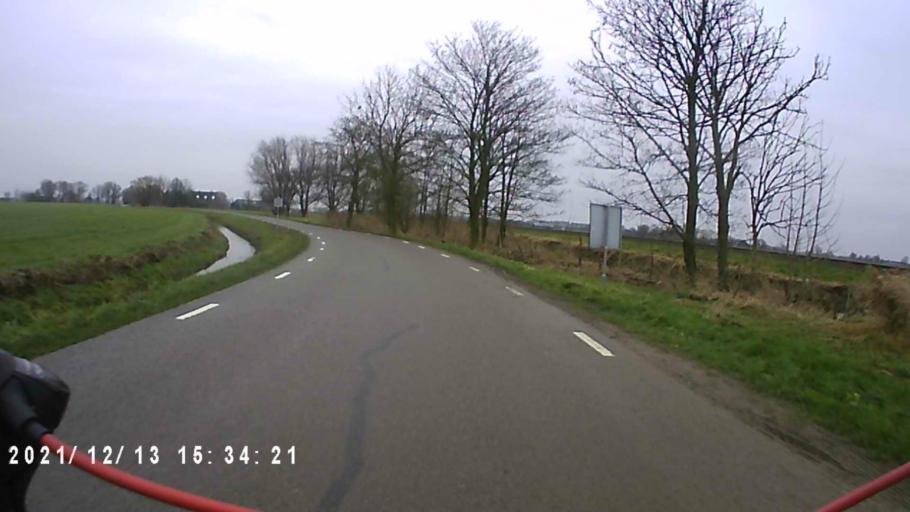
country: NL
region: Groningen
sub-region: Gemeente Appingedam
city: Appingedam
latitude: 53.3293
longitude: 6.8184
